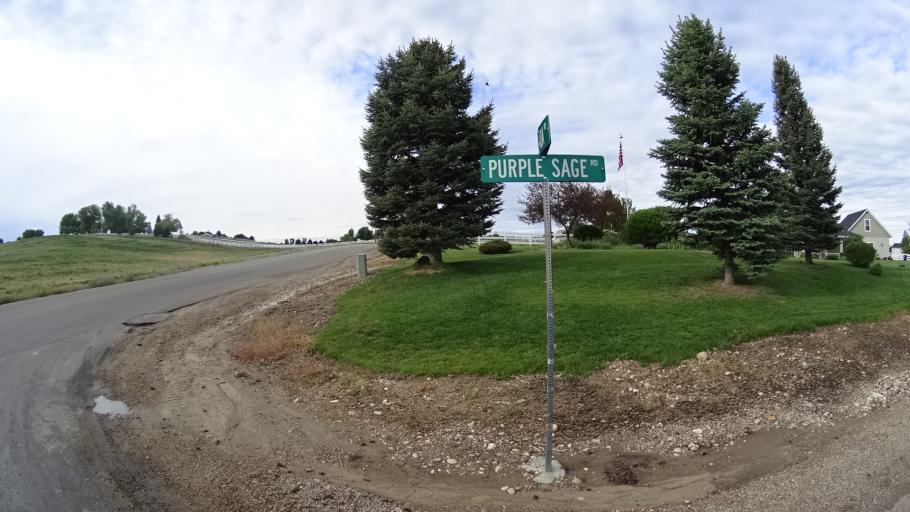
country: US
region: Idaho
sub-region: Ada County
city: Star
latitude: 43.7374
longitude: -116.5129
